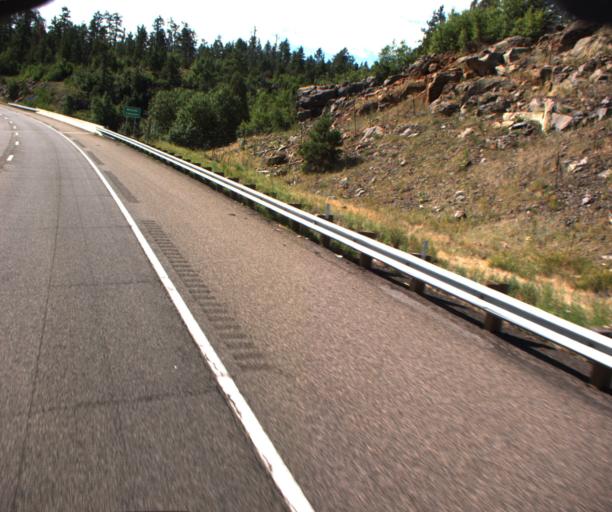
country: US
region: Arizona
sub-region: Coconino County
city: Sedona
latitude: 34.8658
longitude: -111.6273
